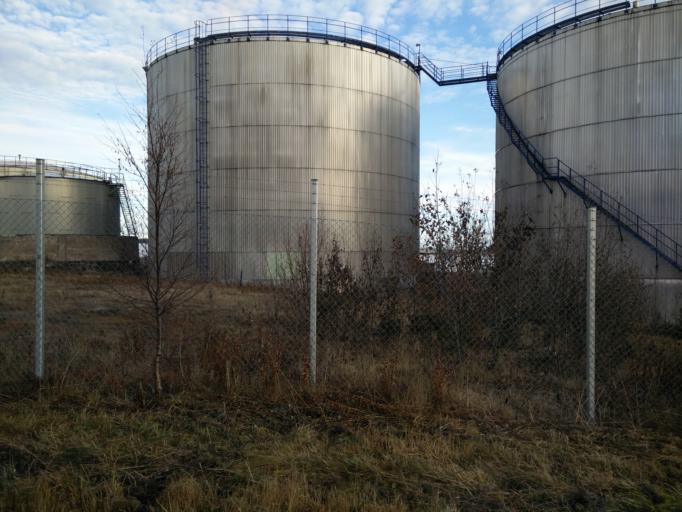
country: SE
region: Vaesternorrland
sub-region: Haernoesands Kommun
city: Haernoesand
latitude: 62.6439
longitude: 17.9338
